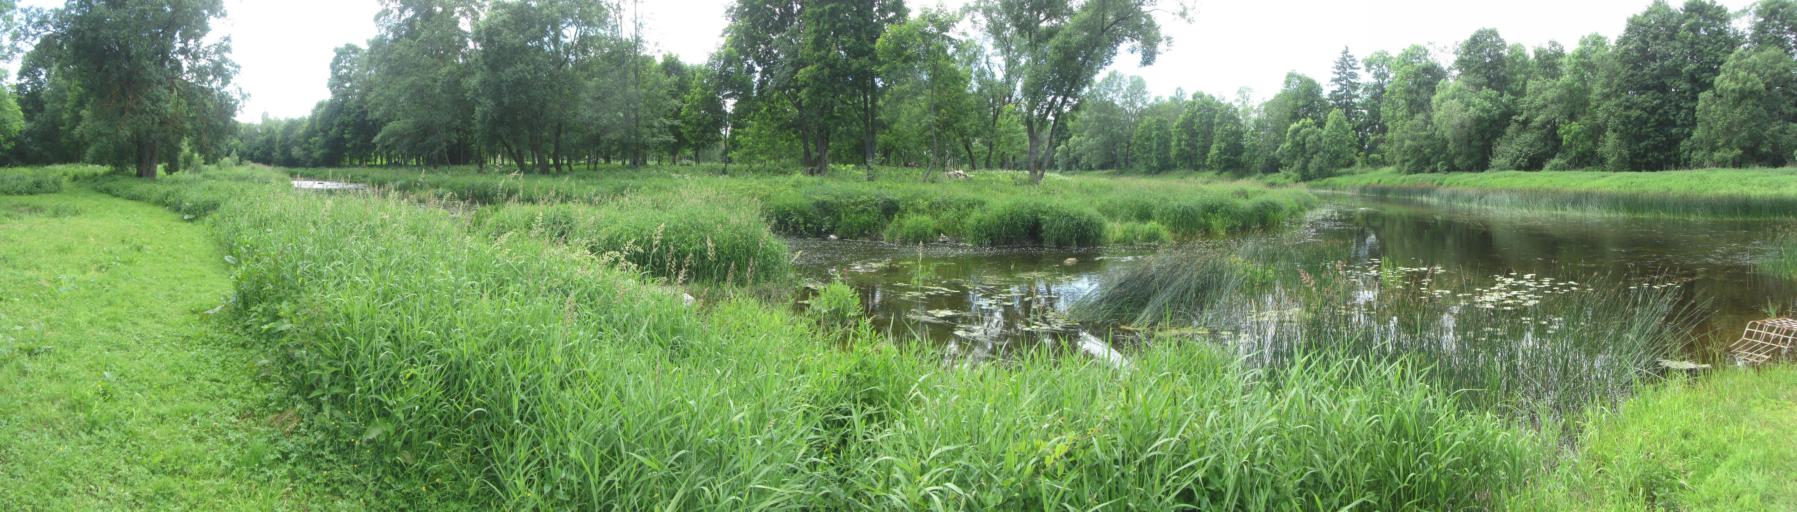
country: LT
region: Panevezys
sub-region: Birzai
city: Birzai
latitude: 56.4007
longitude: 24.7693
